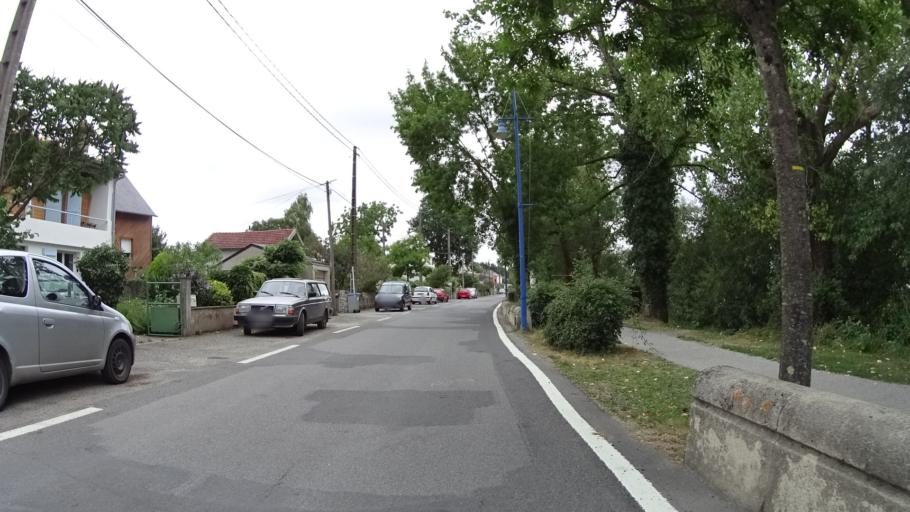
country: FR
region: Pays de la Loire
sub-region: Departement de la Loire-Atlantique
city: Sainte-Luce-sur-Loire
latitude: 47.2356
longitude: -1.4733
